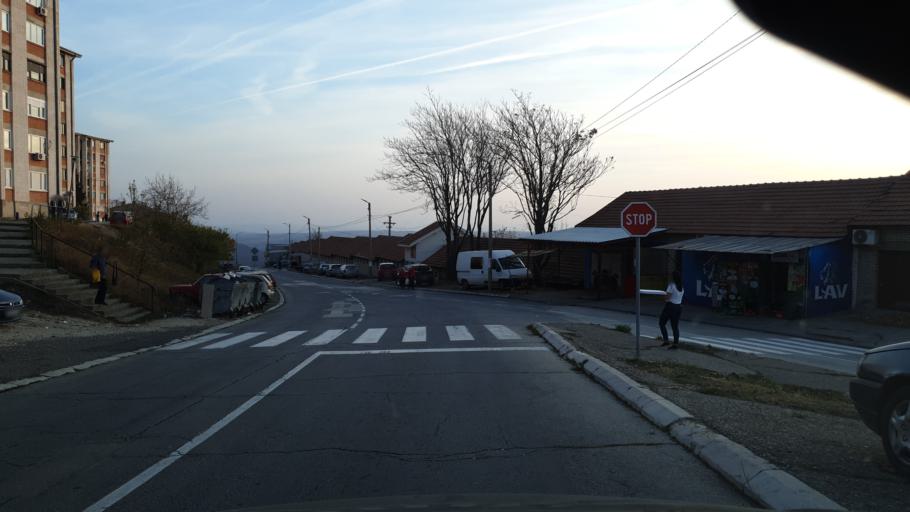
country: RS
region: Central Serbia
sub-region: Borski Okrug
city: Bor
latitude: 44.0572
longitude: 22.0952
